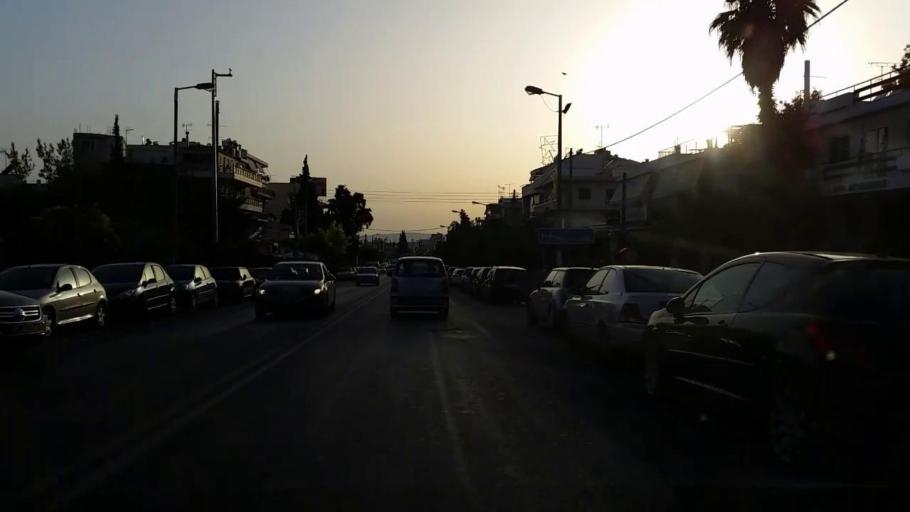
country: GR
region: Attica
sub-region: Nomarchia Athinas
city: Argyroupoli
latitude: 37.9060
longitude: 23.7489
